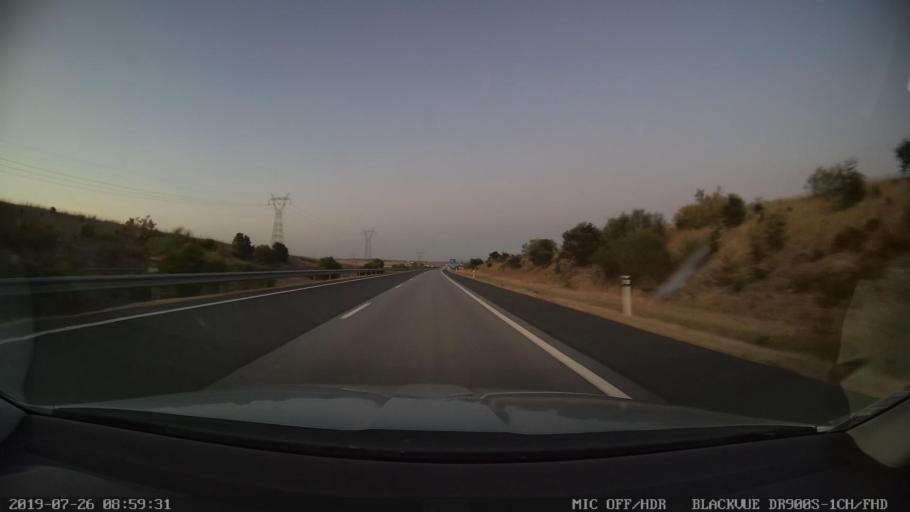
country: PT
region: Evora
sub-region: Evora
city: Evora
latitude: 38.6401
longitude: -7.8716
